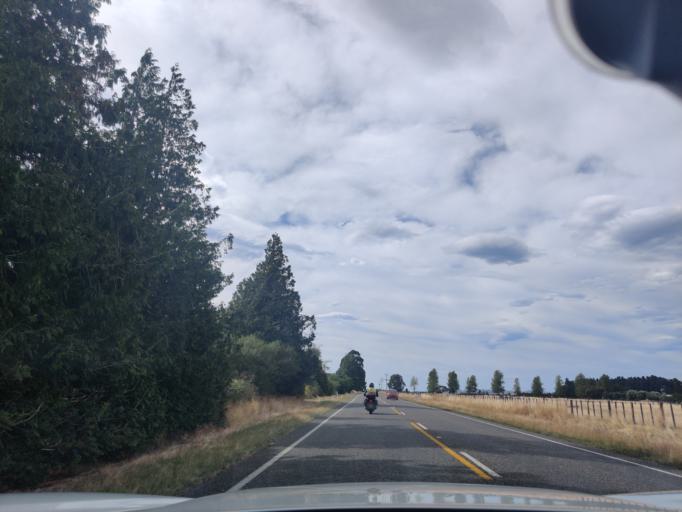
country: NZ
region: Wellington
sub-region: Masterton District
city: Masterton
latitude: -40.8727
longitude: 175.6502
